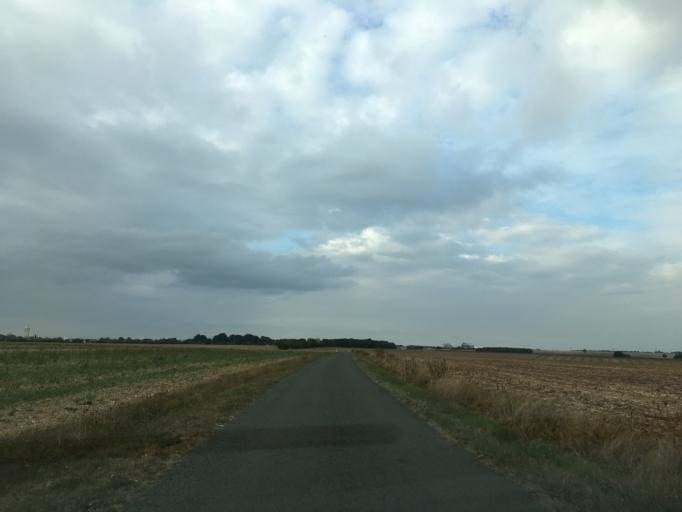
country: FR
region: Poitou-Charentes
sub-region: Departement des Deux-Sevres
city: Beauvoir-sur-Niort
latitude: 46.0806
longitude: -0.4984
